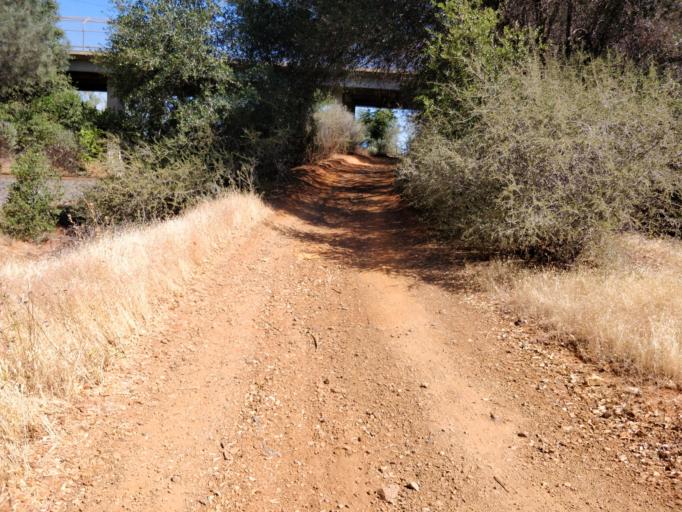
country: US
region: California
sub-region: Shasta County
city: Central Valley (historical)
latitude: 40.6628
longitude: -122.3936
